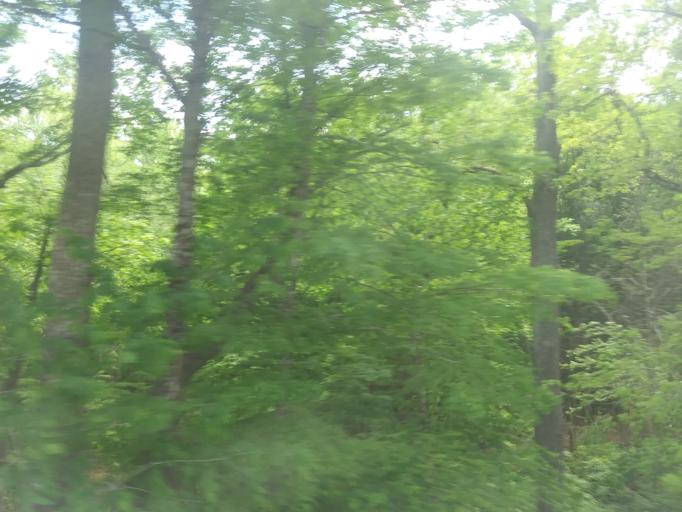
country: US
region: Massachusetts
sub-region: Franklin County
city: Buckland
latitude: 42.5809
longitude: -72.8185
